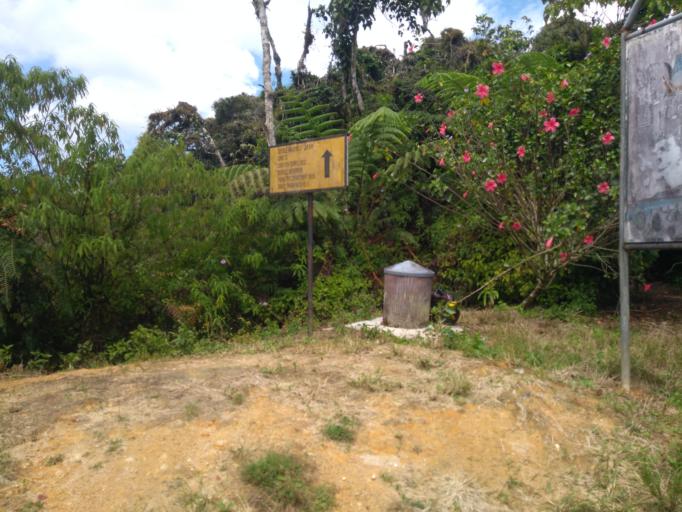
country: MY
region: Pahang
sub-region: Cameron Highlands
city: Tanah Rata
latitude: 4.4828
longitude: 101.3851
